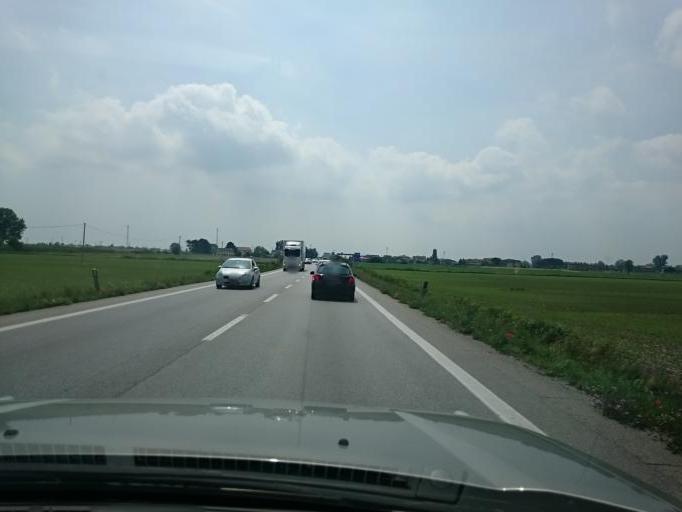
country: IT
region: Veneto
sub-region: Provincia di Padova
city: Codevigo
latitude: 45.2510
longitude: 12.1345
